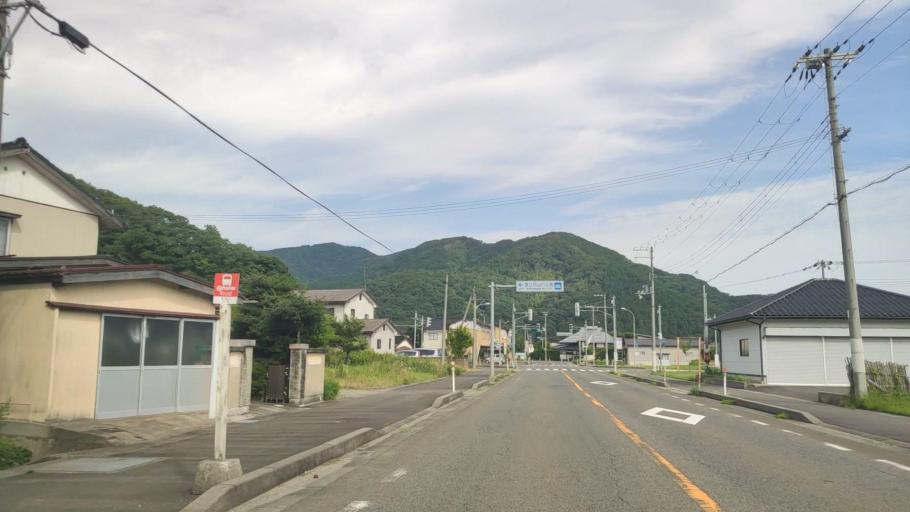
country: JP
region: Hyogo
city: Toyooka
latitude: 35.6419
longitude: 134.8337
